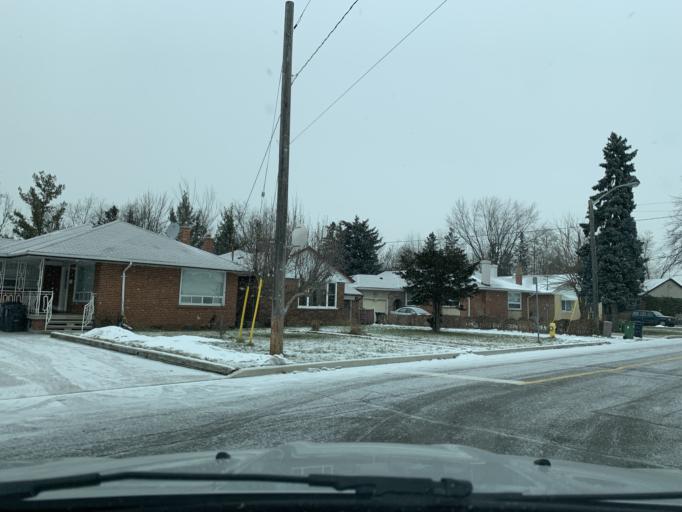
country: CA
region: Ontario
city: Concord
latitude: 43.7337
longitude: -79.4940
